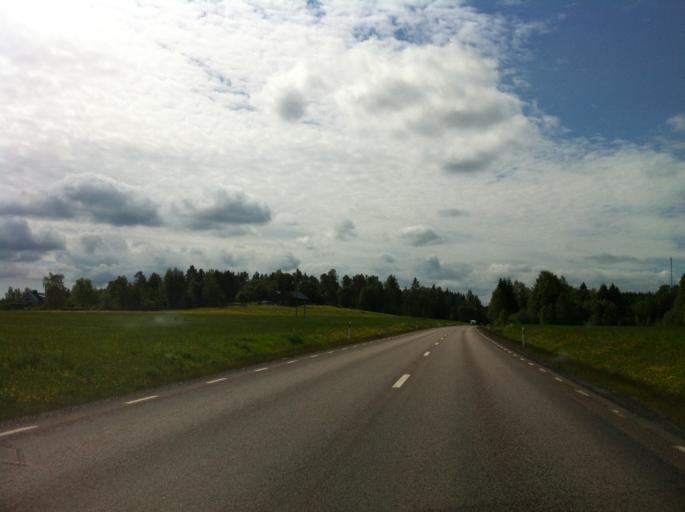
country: SE
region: Vaermland
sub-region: Karlstads Kommun
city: Edsvalla
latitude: 59.4614
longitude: 13.2138
